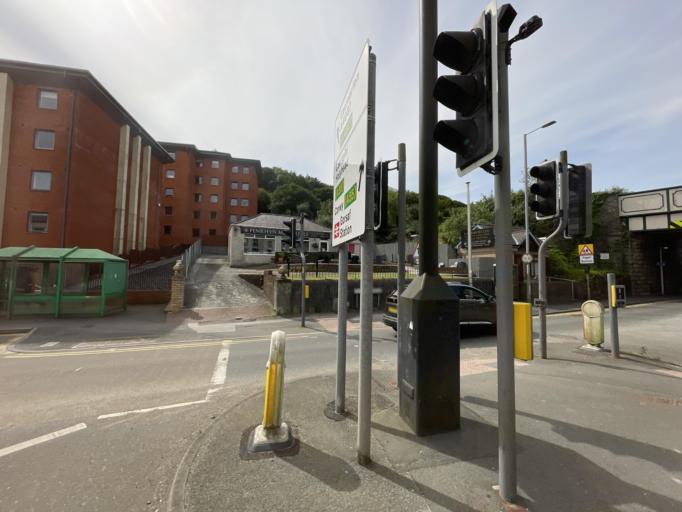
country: GB
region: Wales
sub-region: Gwynedd
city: Bangor
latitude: 53.2225
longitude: -4.1331
